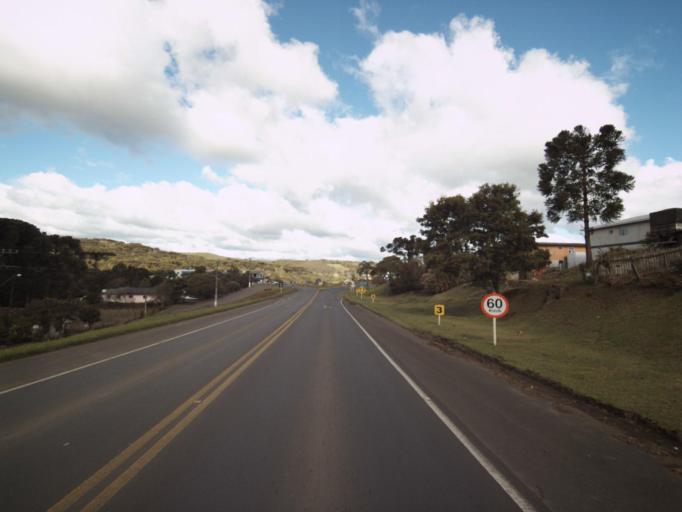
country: BR
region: Santa Catarina
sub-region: Joacaba
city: Joacaba
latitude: -27.0023
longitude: -51.7408
